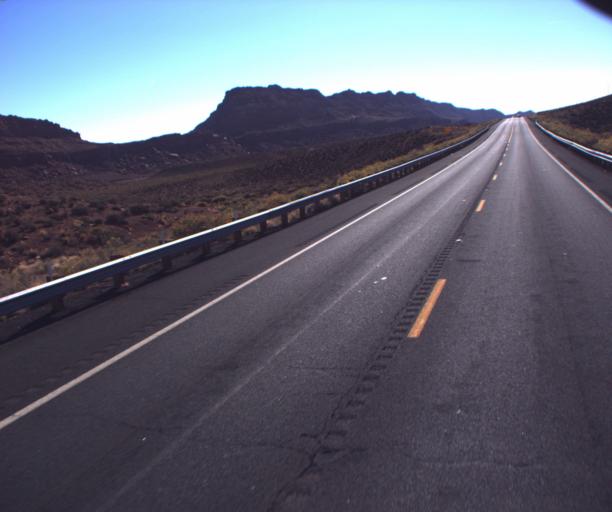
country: US
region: Arizona
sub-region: Coconino County
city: Tuba City
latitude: 36.2698
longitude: -111.4331
